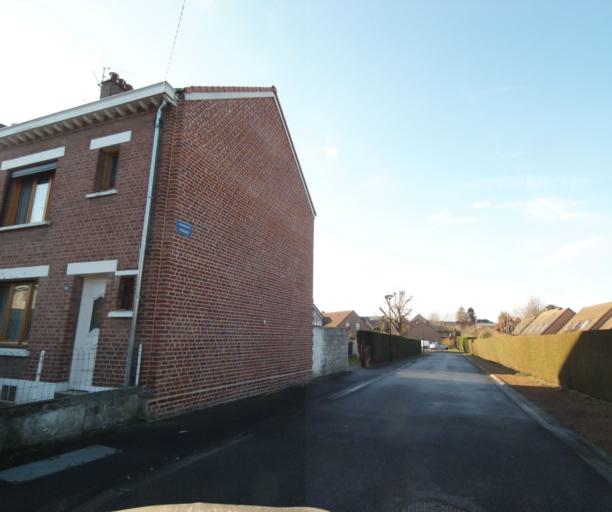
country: FR
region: Nord-Pas-de-Calais
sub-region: Departement du Nord
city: Valenciennes
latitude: 50.3426
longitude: 3.5302
